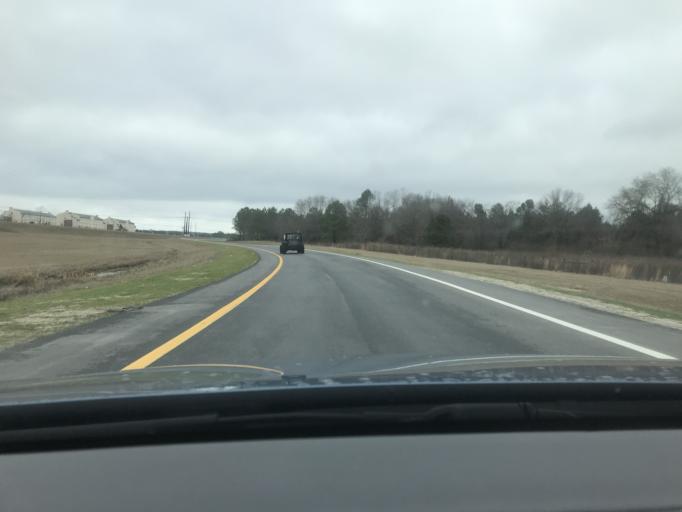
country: US
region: North Carolina
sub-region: Cumberland County
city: Fort Bragg
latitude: 35.0643
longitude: -79.0218
